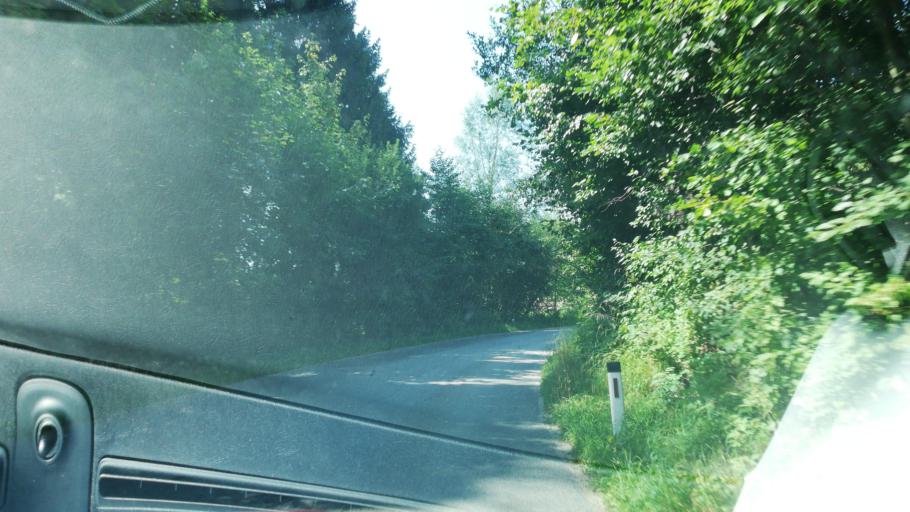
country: AT
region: Upper Austria
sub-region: Politischer Bezirk Urfahr-Umgebung
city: Feldkirchen an der Donau
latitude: 48.3404
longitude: 13.9666
